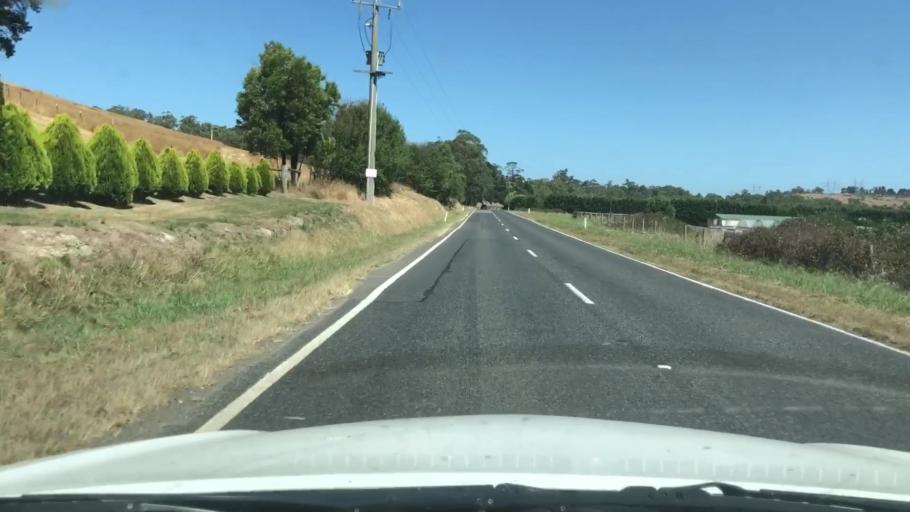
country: AU
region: Victoria
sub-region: Yarra Ranges
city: Woori Yallock
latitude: -37.7948
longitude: 145.5228
